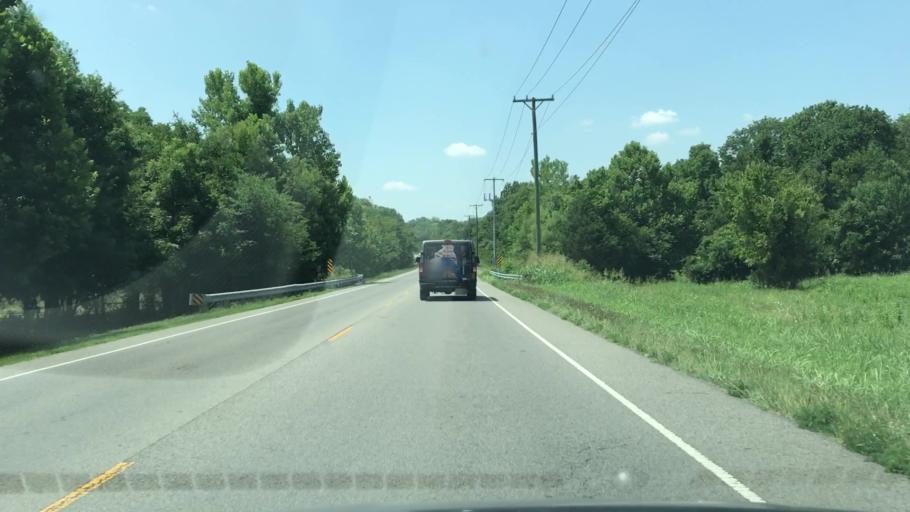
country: US
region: Tennessee
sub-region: Rutherford County
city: La Vergne
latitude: 36.0009
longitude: -86.6229
